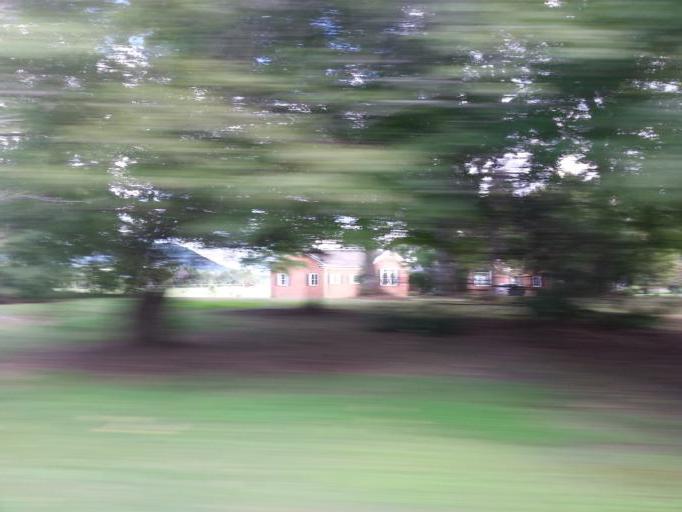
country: US
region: Tennessee
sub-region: Union County
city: Condon
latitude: 36.1132
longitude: -83.8061
